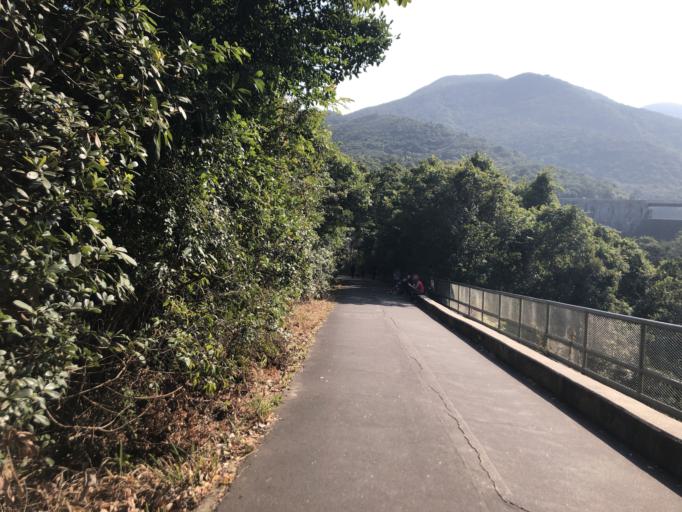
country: HK
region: Wanchai
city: Wan Chai
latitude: 22.2500
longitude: 114.2132
